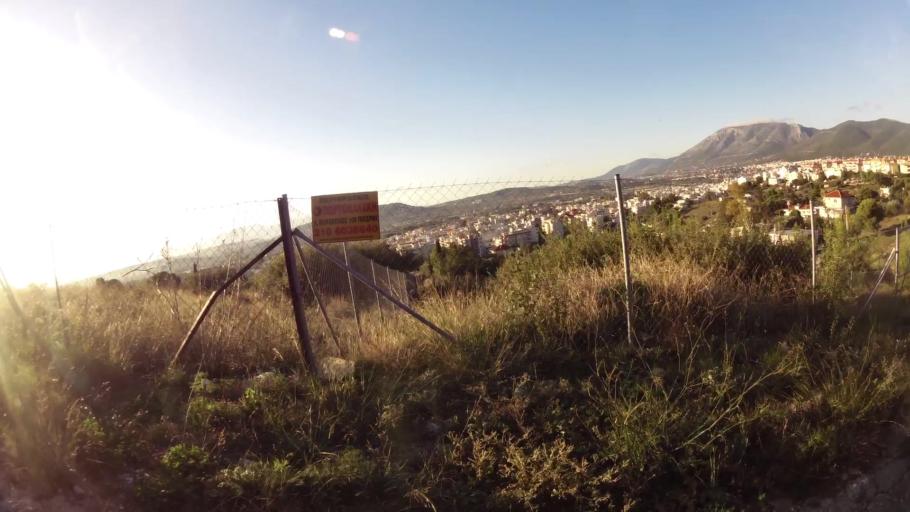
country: GR
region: Attica
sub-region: Nomarchia Anatolikis Attikis
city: Pallini
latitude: 38.0095
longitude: 23.8855
